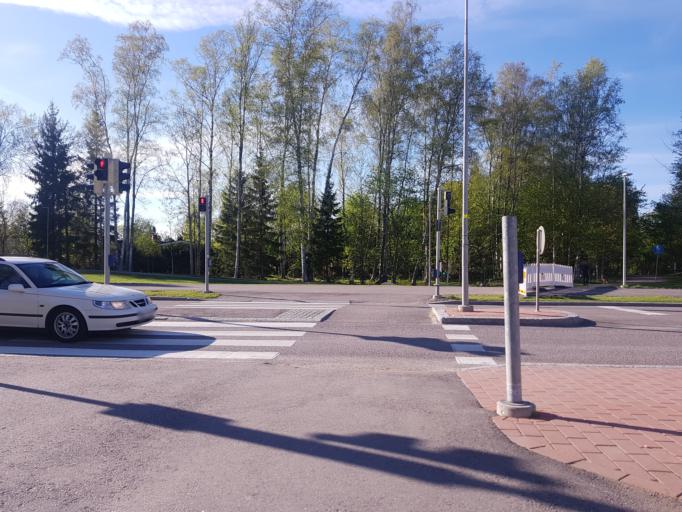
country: FI
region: Uusimaa
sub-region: Helsinki
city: Vantaa
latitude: 60.2782
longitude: 25.0278
